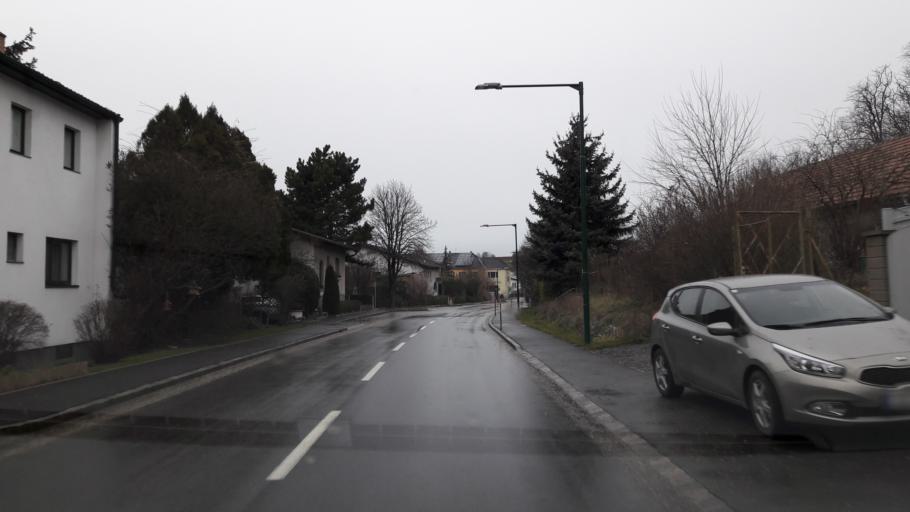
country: AT
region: Lower Austria
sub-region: Politischer Bezirk Mistelbach
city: Hochleithen
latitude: 48.4453
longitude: 16.5289
